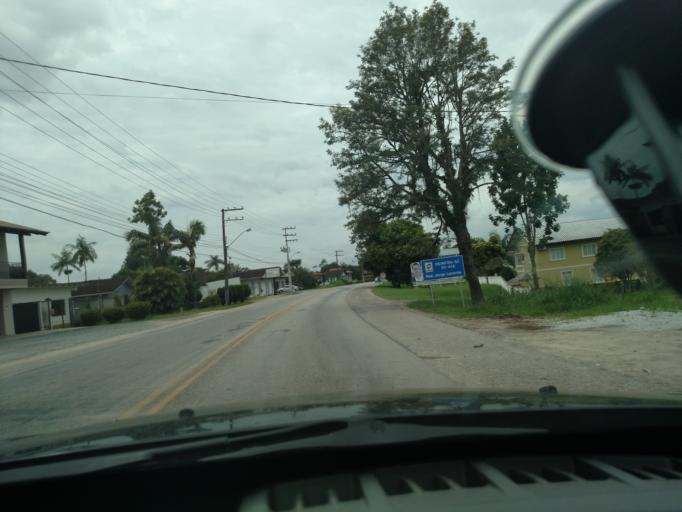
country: BR
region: Santa Catarina
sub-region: Gaspar
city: Gaspar
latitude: -26.9096
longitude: -48.9323
